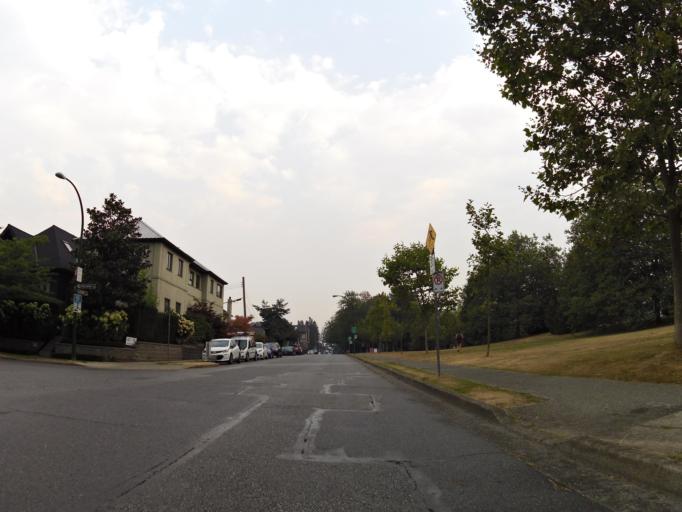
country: CA
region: British Columbia
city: West End
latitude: 49.2743
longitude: -123.1463
